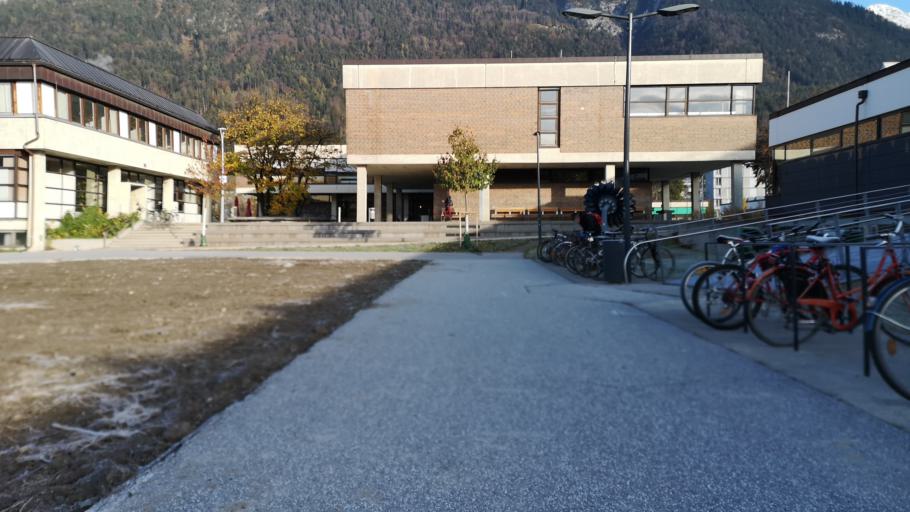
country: AT
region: Tyrol
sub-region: Politischer Bezirk Innsbruck Land
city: Vols
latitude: 47.2634
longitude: 11.3440
